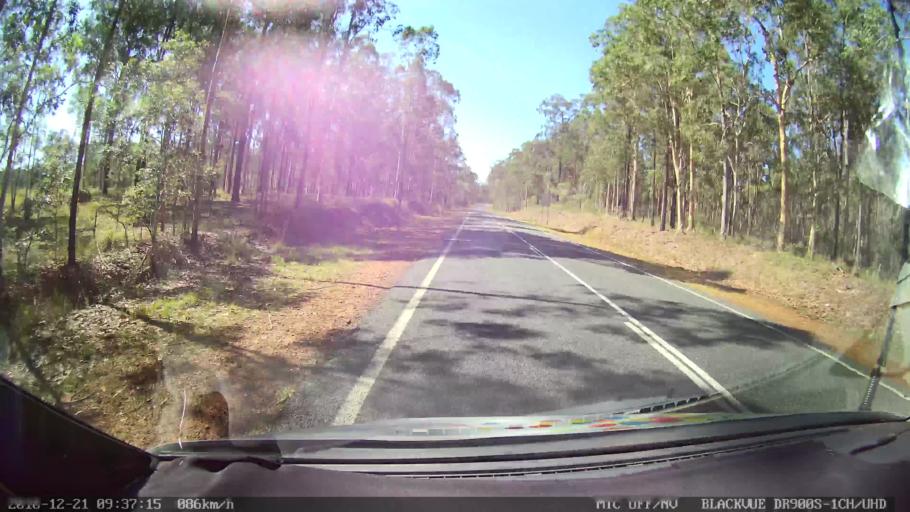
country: AU
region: New South Wales
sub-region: Clarence Valley
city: Grafton
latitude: -29.5340
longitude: 152.9860
